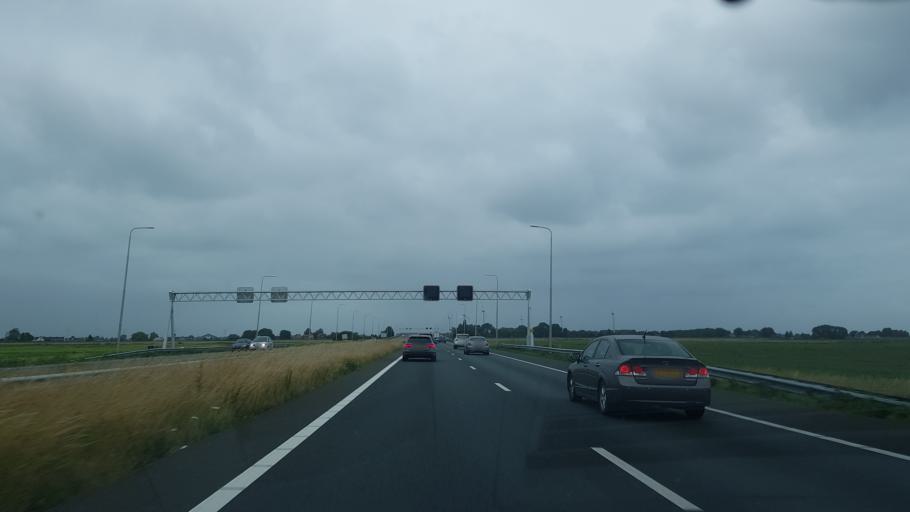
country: NL
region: North Holland
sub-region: Gemeente Hoorn
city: Hoorn
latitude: 52.5943
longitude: 4.9884
